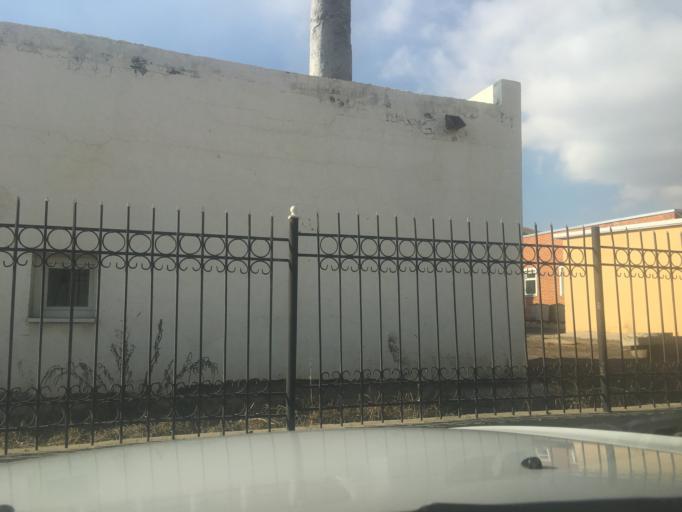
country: MN
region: Ulaanbaatar
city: Ulaanbaatar
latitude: 47.9671
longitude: 106.8266
